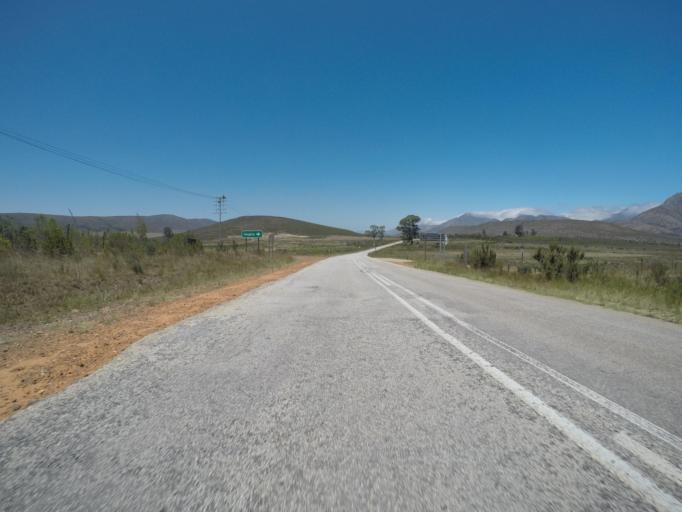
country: ZA
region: Eastern Cape
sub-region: Cacadu District Municipality
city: Kareedouw
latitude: -33.8521
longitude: 23.9812
